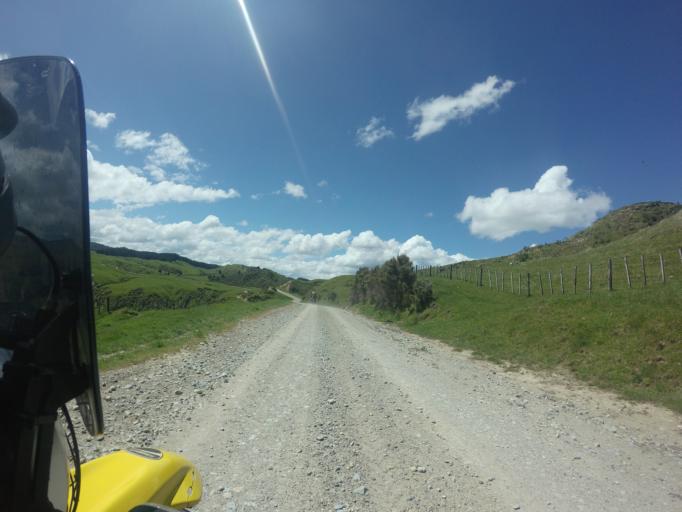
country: NZ
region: Hawke's Bay
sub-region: Wairoa District
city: Wairoa
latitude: -38.9534
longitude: 177.7223
